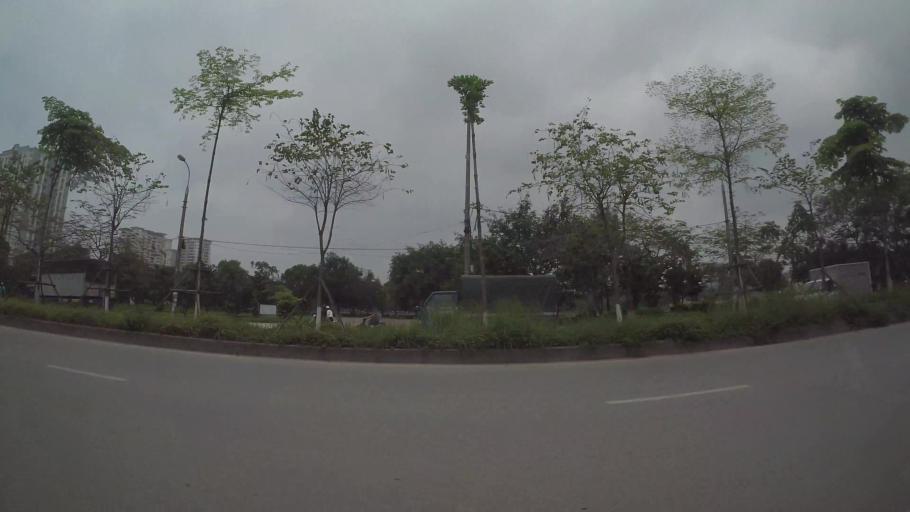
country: VN
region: Ha Noi
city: Hai BaTrung
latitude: 20.9835
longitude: 105.8552
